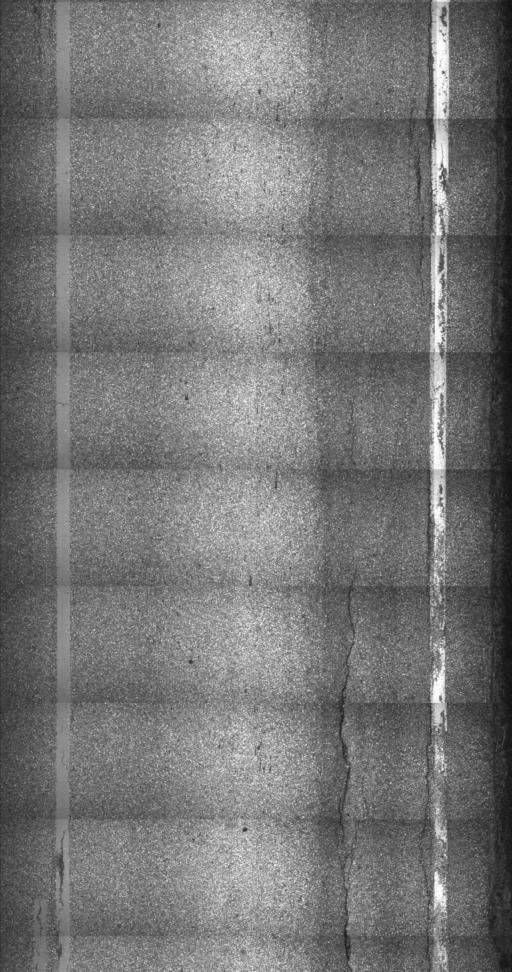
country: US
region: Vermont
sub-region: Franklin County
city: Enosburg Falls
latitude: 44.9595
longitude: -72.9064
